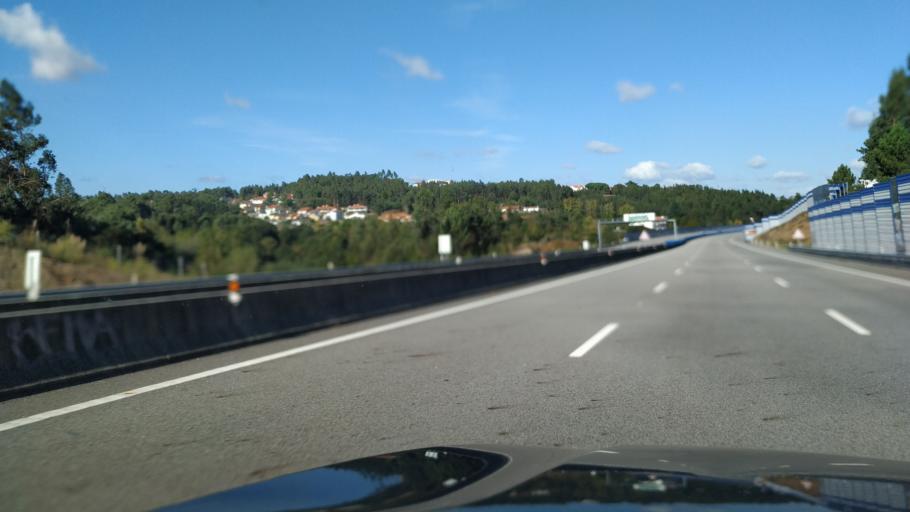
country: PT
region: Porto
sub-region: Vila Nova de Gaia
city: Olival
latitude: 41.0692
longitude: -8.5340
